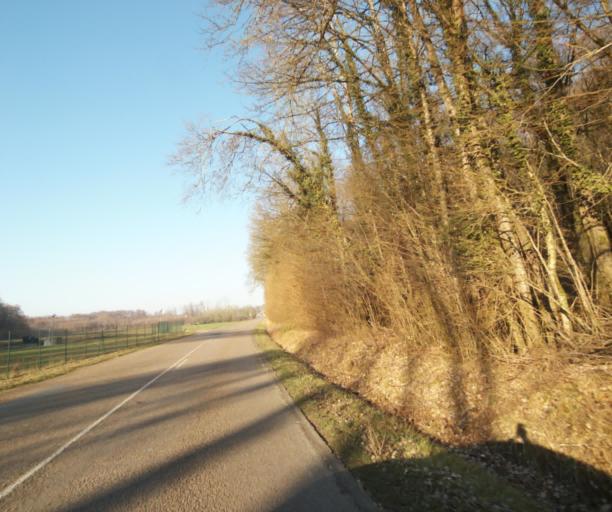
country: FR
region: Champagne-Ardenne
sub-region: Departement de la Haute-Marne
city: Chevillon
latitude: 48.5320
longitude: 5.1066
